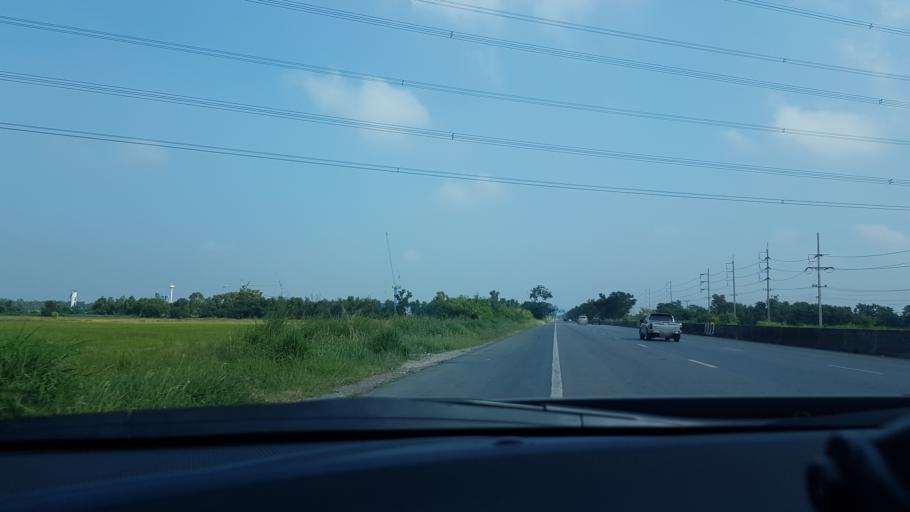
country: TH
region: Pathum Thani
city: Sam Khok
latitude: 14.1317
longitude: 100.5694
